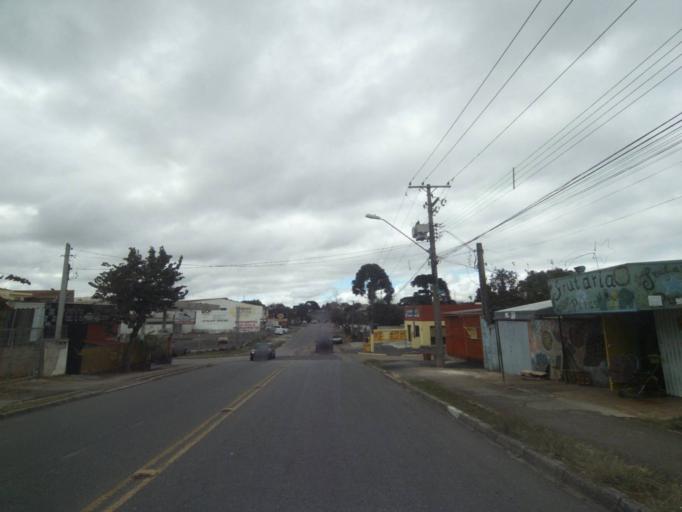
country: BR
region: Parana
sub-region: Sao Jose Dos Pinhais
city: Sao Jose dos Pinhais
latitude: -25.5406
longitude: -49.2908
